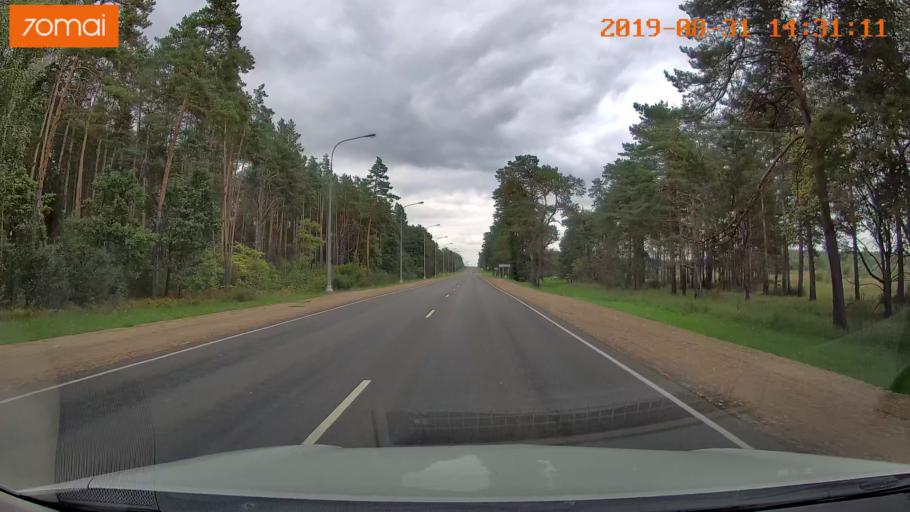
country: RU
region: Smolensk
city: Yekimovichi
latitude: 54.1367
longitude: 33.3680
